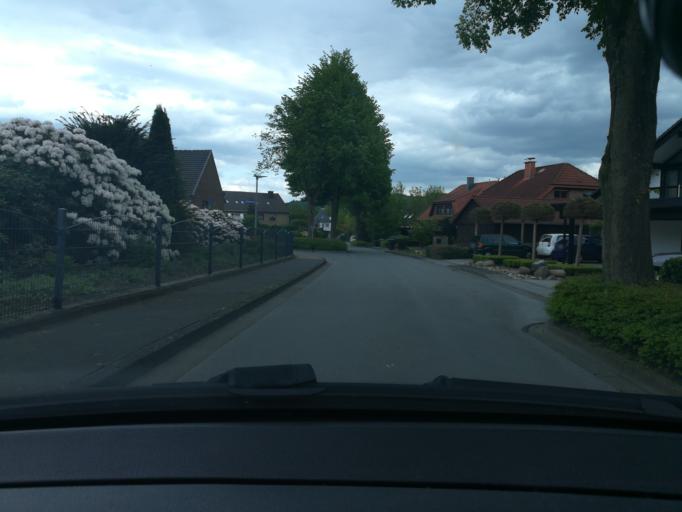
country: DE
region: North Rhine-Westphalia
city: Borgholzhausen
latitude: 52.0971
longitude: 8.2888
